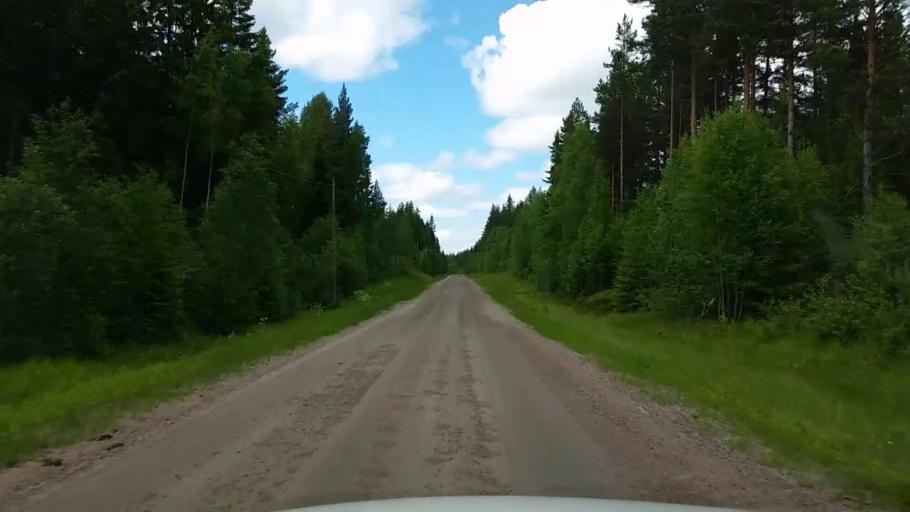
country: SE
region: Gaevleborg
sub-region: Ovanakers Kommun
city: Alfta
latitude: 61.4899
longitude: 15.9856
